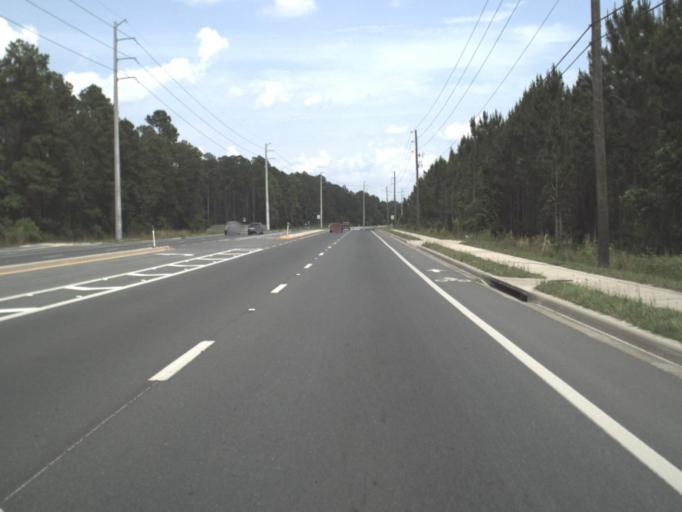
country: US
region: Florida
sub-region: Putnam County
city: Interlachen
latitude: 29.6292
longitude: -81.8222
